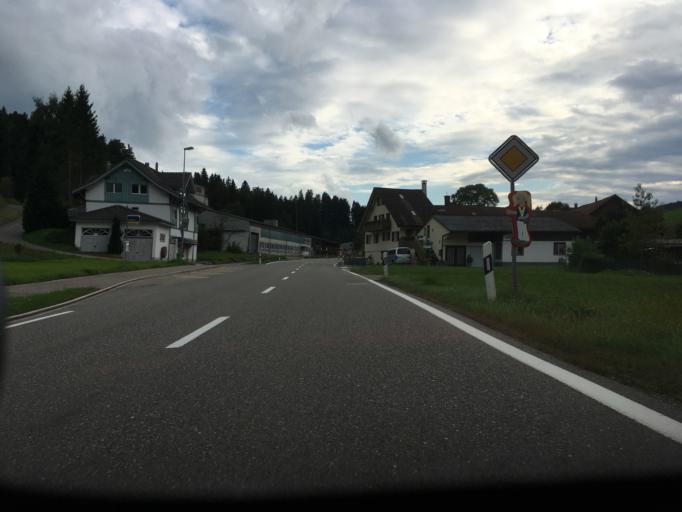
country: CH
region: Zurich
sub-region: Bezirk Pfaeffikon
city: Hittnau / Hittnau (Dorf)
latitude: 47.3856
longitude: 8.8451
